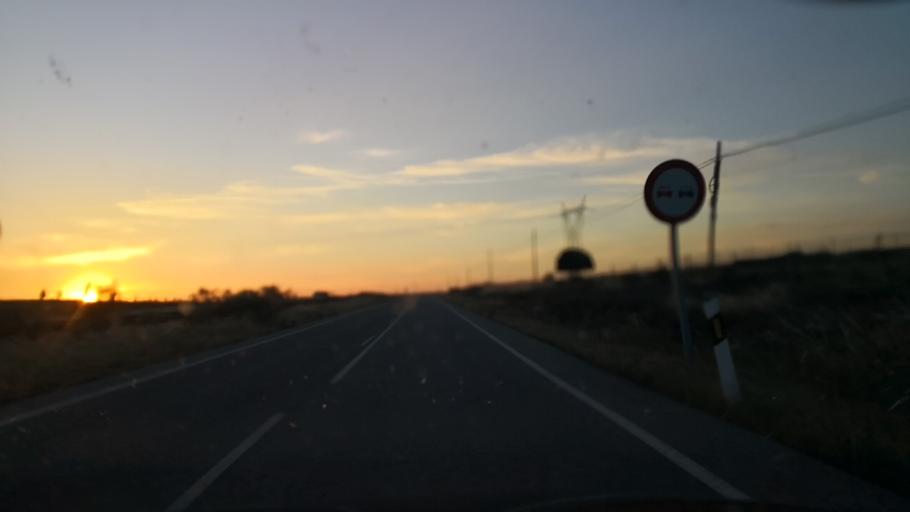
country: ES
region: Extremadura
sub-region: Provincia de Caceres
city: Alcantara
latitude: 39.6980
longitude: -6.8740
